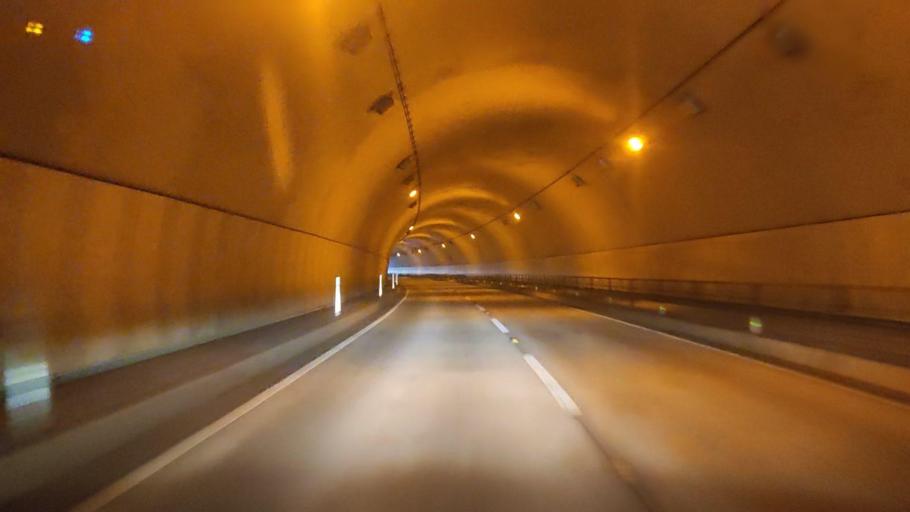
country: JP
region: Miyazaki
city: Nobeoka
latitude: 32.6987
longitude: 131.8142
